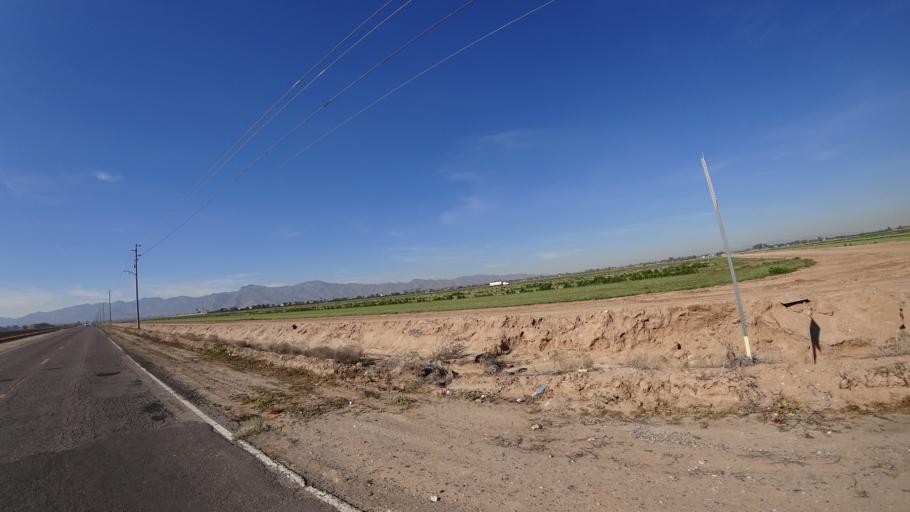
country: US
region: Arizona
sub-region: Maricopa County
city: Citrus Park
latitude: 33.5082
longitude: -112.4355
